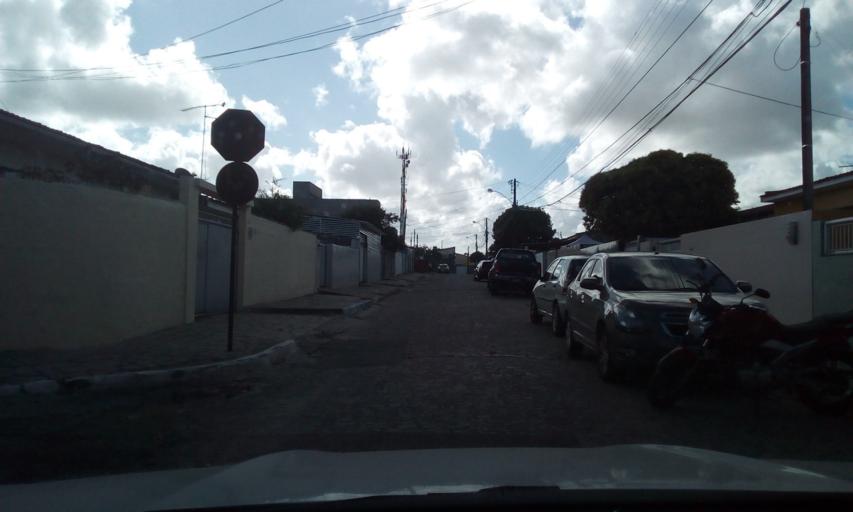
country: BR
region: Paraiba
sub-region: Joao Pessoa
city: Joao Pessoa
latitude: -7.1750
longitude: -34.8378
